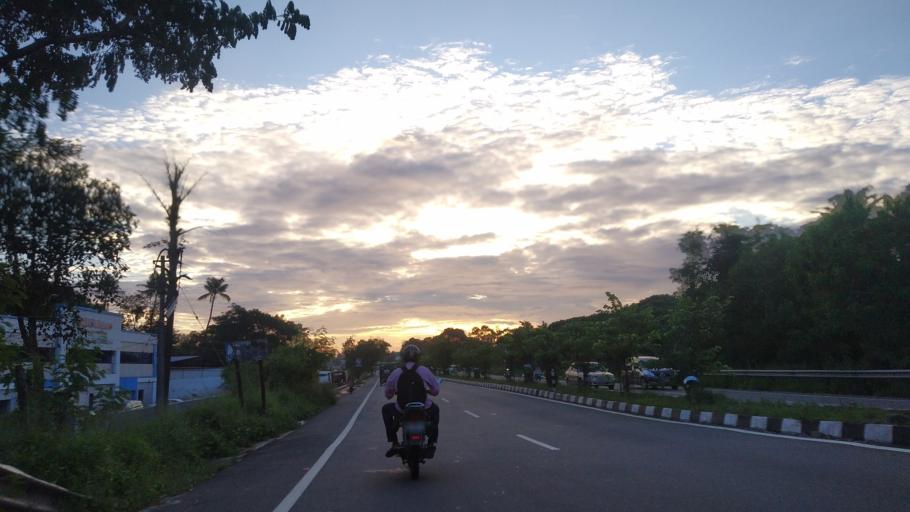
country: IN
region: Kerala
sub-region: Ernakulam
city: Elur
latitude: 10.0631
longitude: 76.2925
